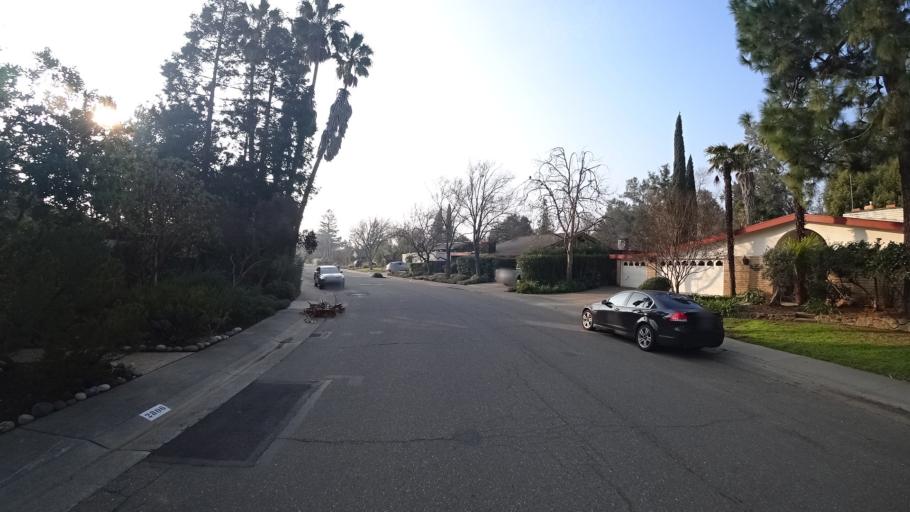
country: US
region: California
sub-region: Yolo County
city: Davis
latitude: 38.5670
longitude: -121.7554
